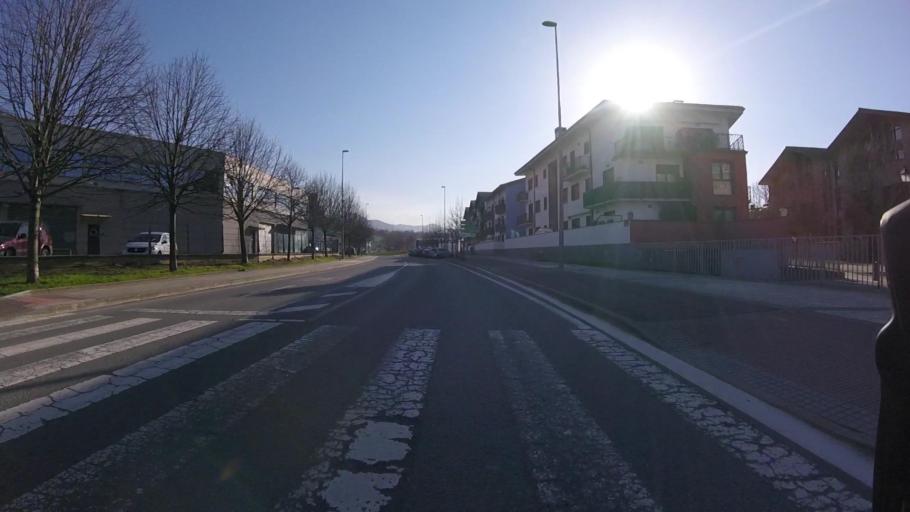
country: ES
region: Basque Country
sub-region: Provincia de Guipuzcoa
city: Astigarraga
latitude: 43.2771
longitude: -1.9537
